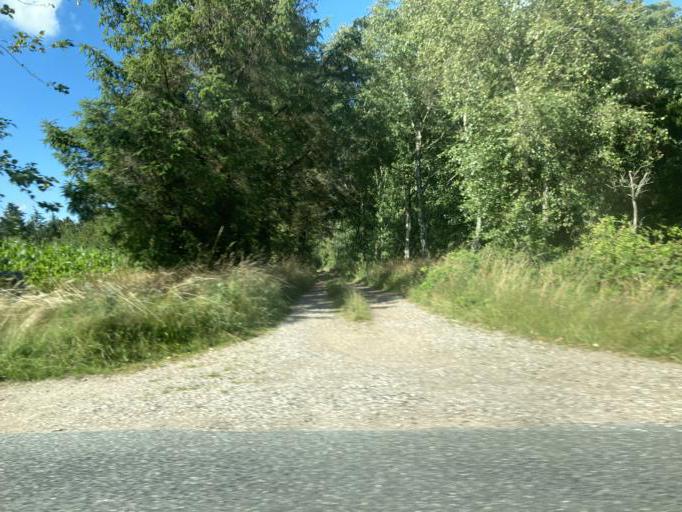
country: DK
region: South Denmark
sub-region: Esbjerg Kommune
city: Ribe
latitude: 55.2882
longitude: 8.7023
